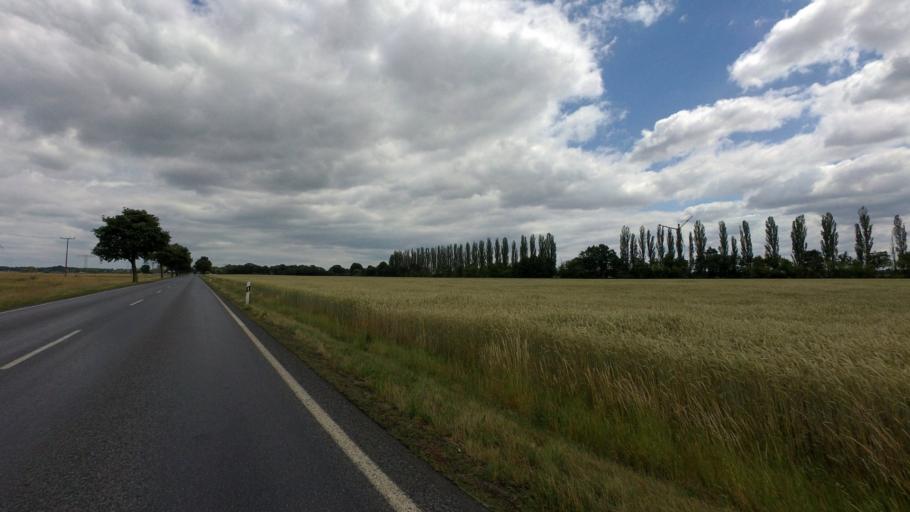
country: DE
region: Brandenburg
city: Luckau
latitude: 51.8535
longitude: 13.6512
